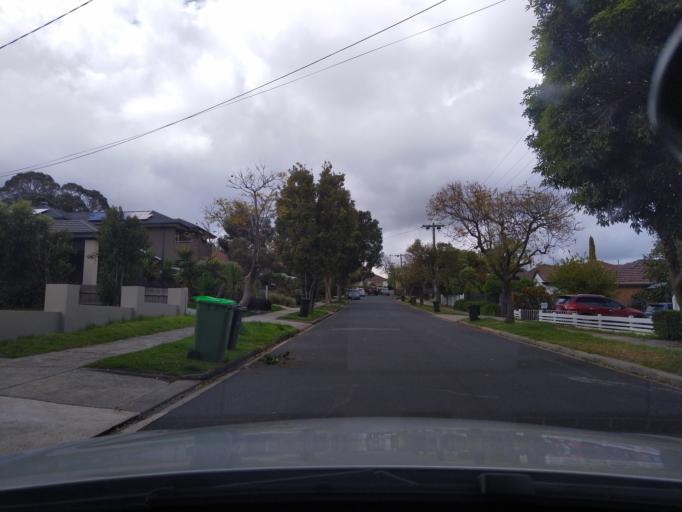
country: AU
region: Victoria
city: Rosanna
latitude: -37.7451
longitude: 145.0737
